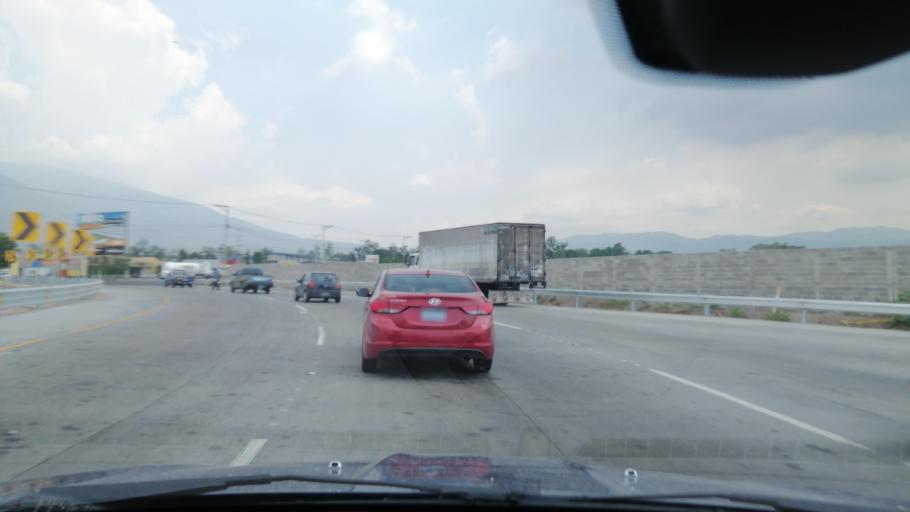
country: SV
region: La Libertad
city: Ciudad Arce
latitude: 13.7784
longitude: -89.3743
